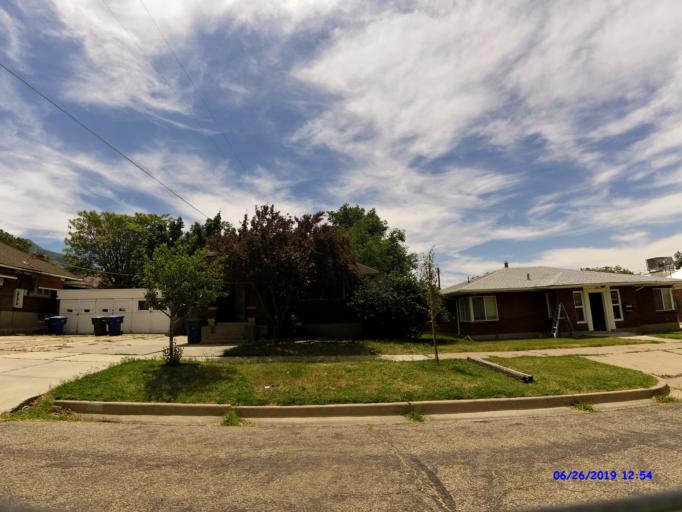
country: US
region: Utah
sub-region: Weber County
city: Ogden
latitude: 41.2245
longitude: -111.9518
